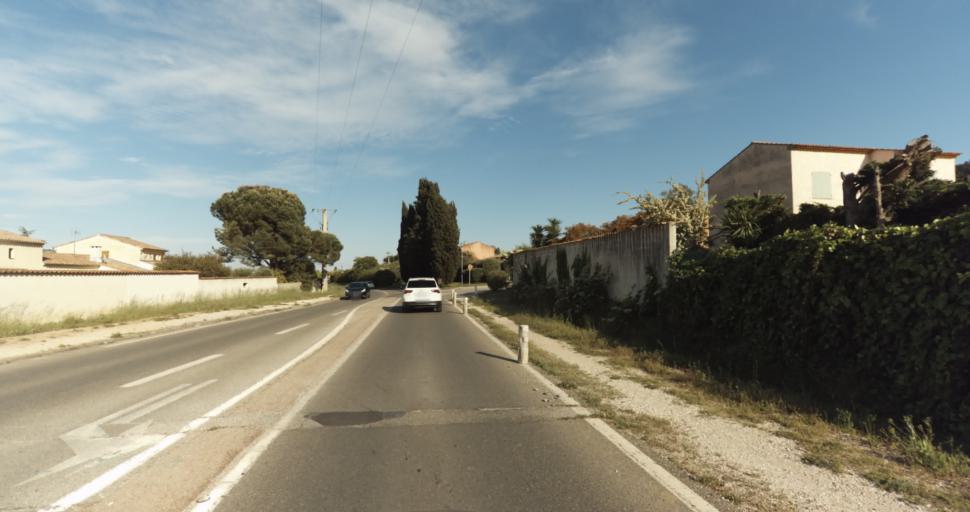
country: FR
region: Provence-Alpes-Cote d'Azur
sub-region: Departement du Var
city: Carqueiranne
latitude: 43.1177
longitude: 6.0799
